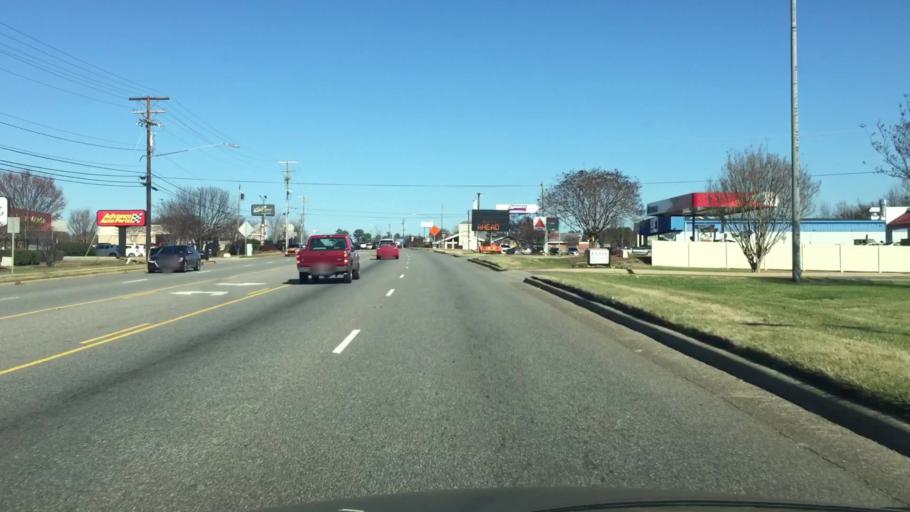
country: US
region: North Carolina
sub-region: Iredell County
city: Mooresville
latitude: 35.5974
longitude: -80.8141
